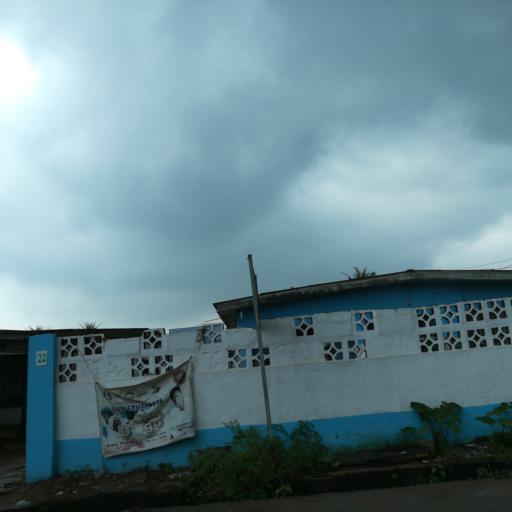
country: NG
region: Lagos
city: Agege
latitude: 6.5904
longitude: 3.2958
